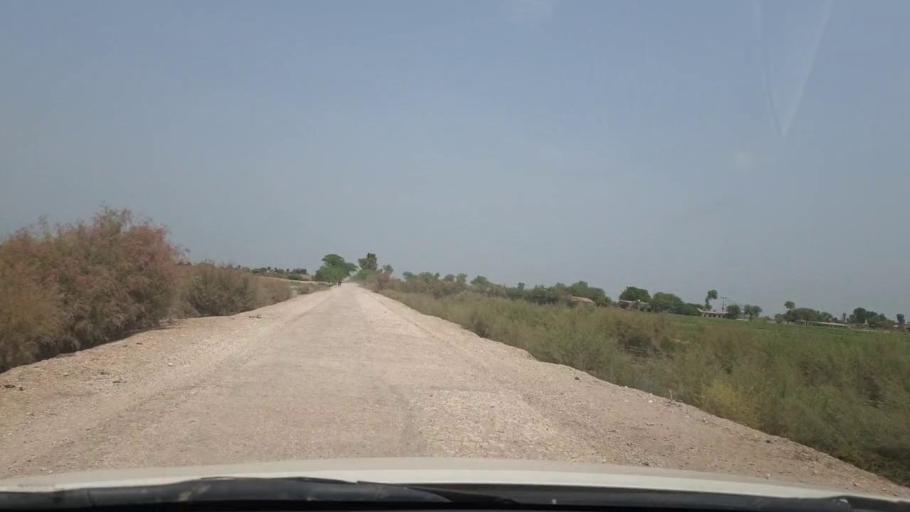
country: PK
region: Sindh
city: Rustam jo Goth
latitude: 28.0414
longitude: 68.8146
